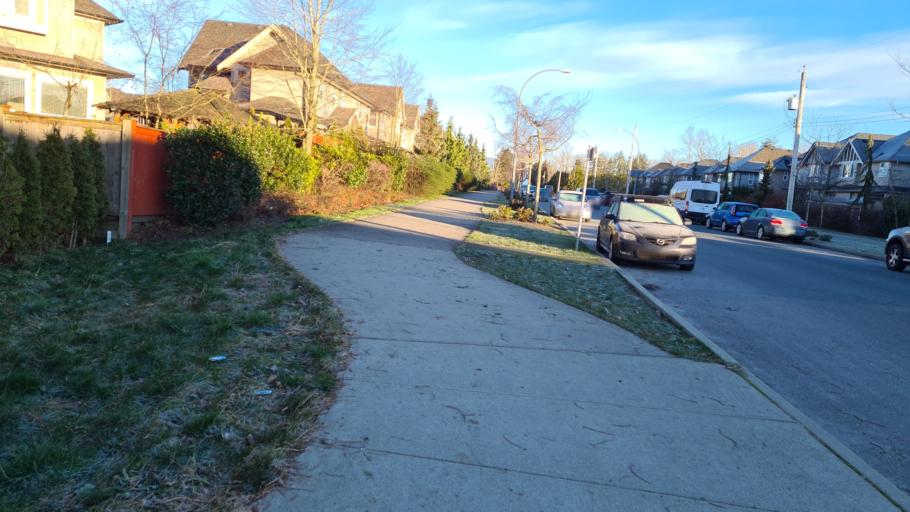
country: CA
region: British Columbia
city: Langley
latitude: 49.1340
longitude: -122.6724
